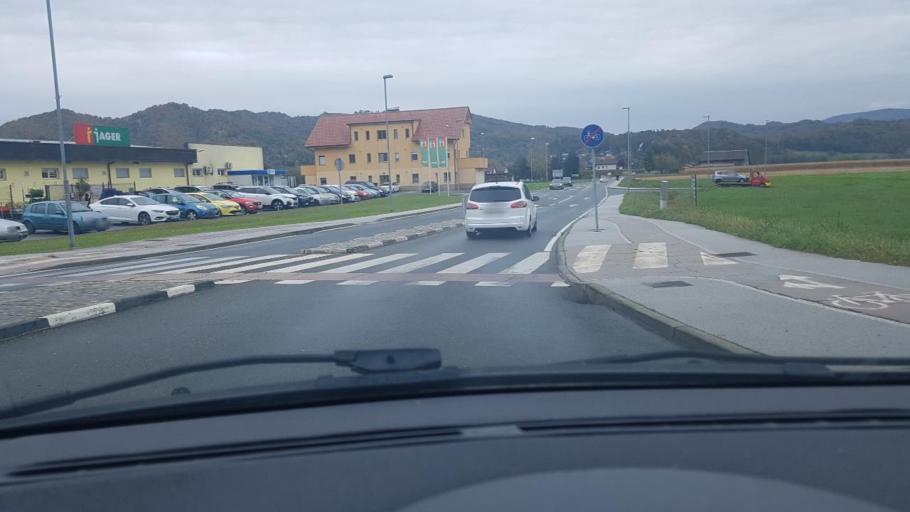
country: SI
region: Majsperk
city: Majsperk
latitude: 46.3474
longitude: 15.7387
